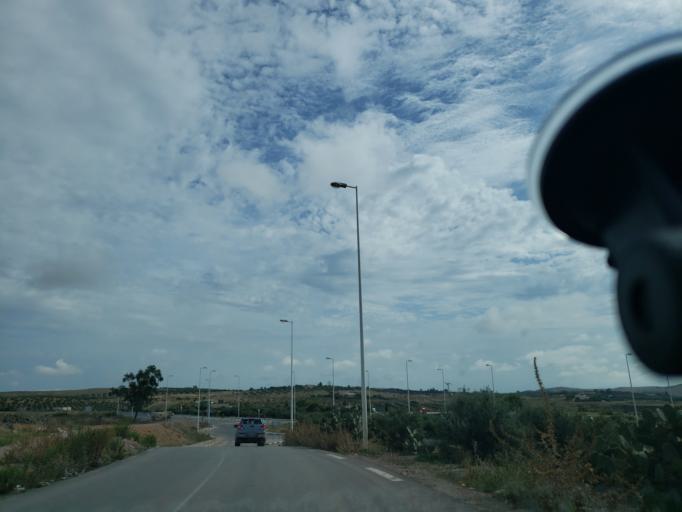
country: TN
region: Zaghwan
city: El Fahs
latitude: 36.3951
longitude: 9.9097
